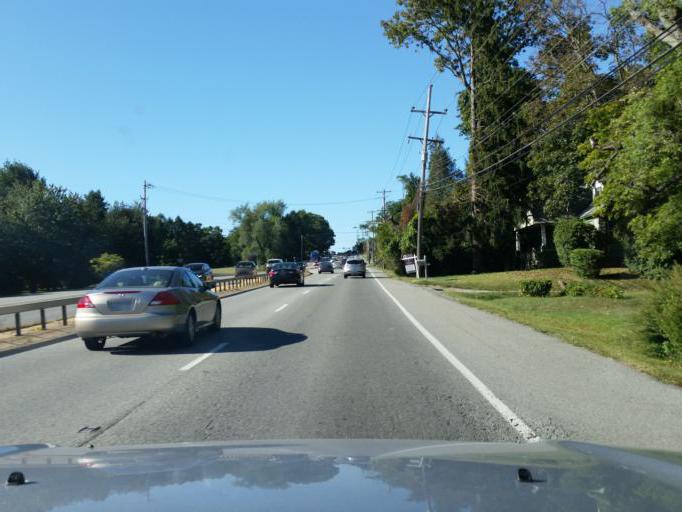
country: US
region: Pennsylvania
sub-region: Chester County
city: West Chester
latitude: 39.9251
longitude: -75.5817
